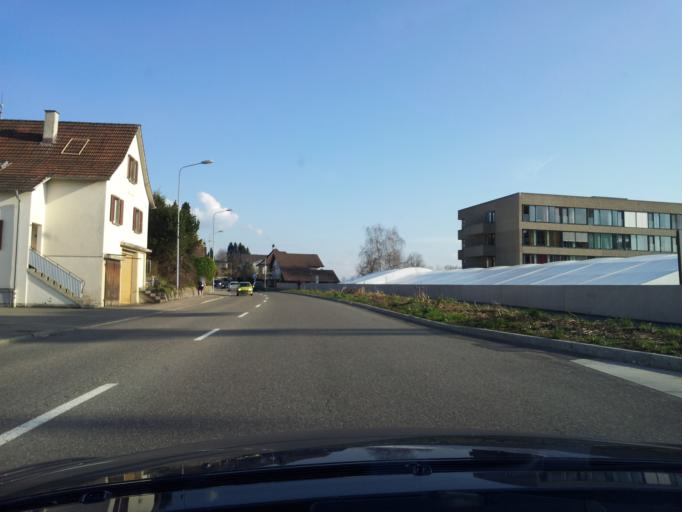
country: CH
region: Aargau
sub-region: Bezirk Baden
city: Kunten
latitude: 47.3885
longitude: 8.3440
